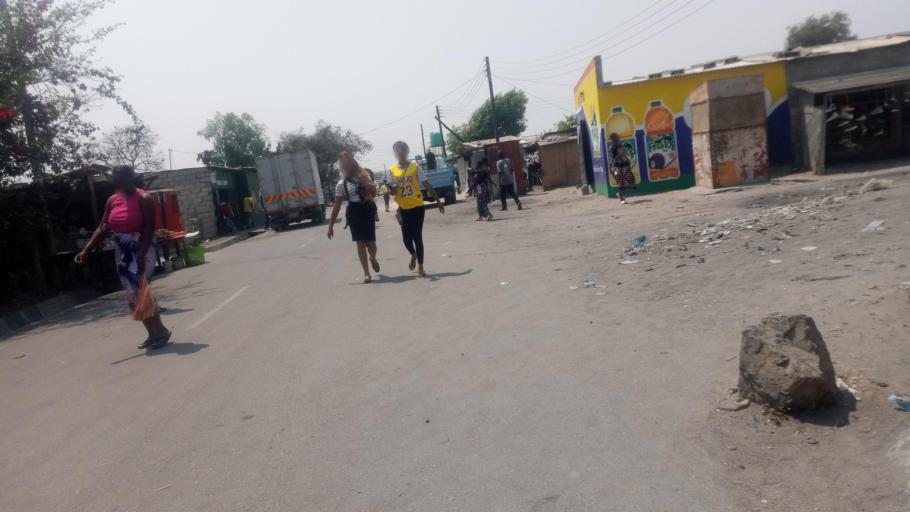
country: ZM
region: Lusaka
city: Lusaka
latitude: -15.4448
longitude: 28.3781
